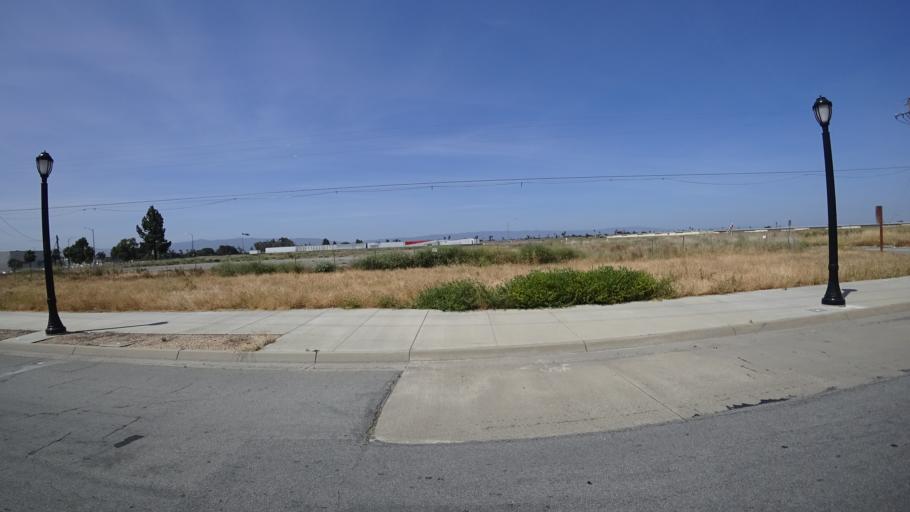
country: US
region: California
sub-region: Santa Clara County
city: Alum Rock
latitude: 37.3319
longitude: -121.8135
